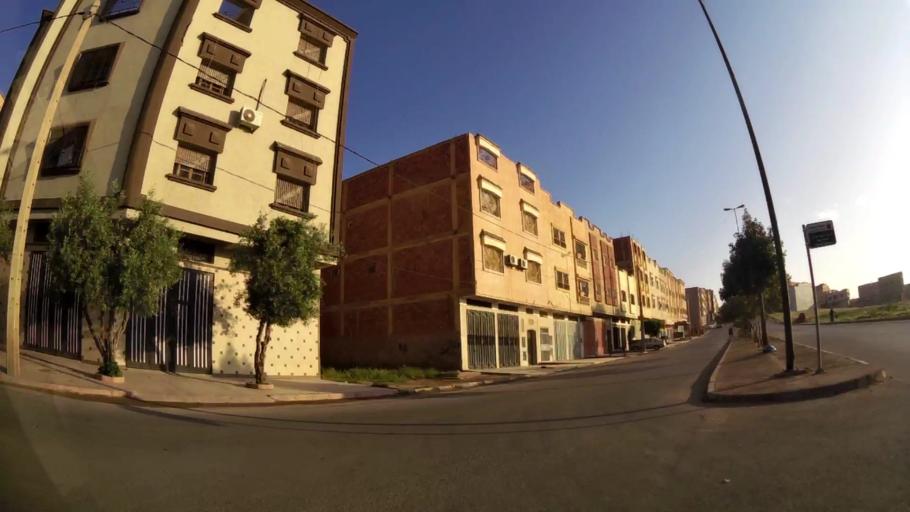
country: MA
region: Oriental
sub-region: Oujda-Angad
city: Oujda
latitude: 34.6729
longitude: -1.9398
